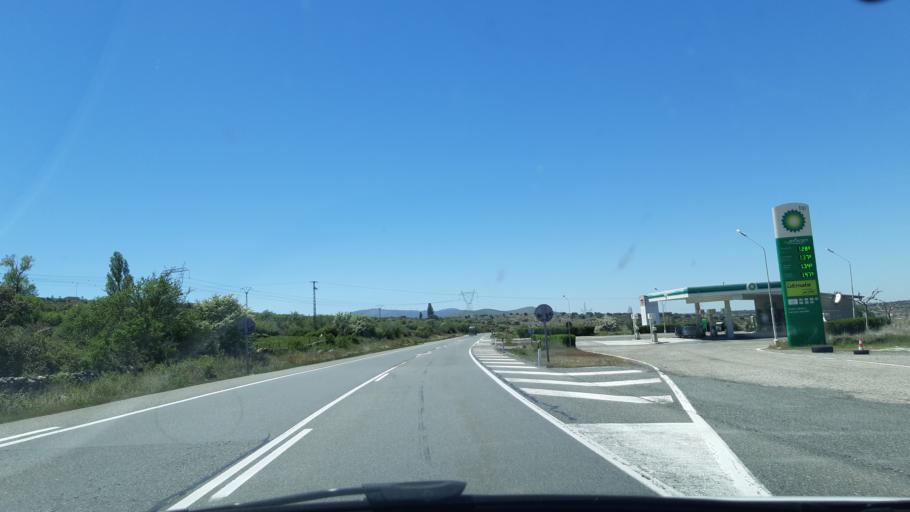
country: ES
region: Castille and Leon
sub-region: Provincia de Segovia
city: Vegas de Matute
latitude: 40.7492
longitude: -4.2965
